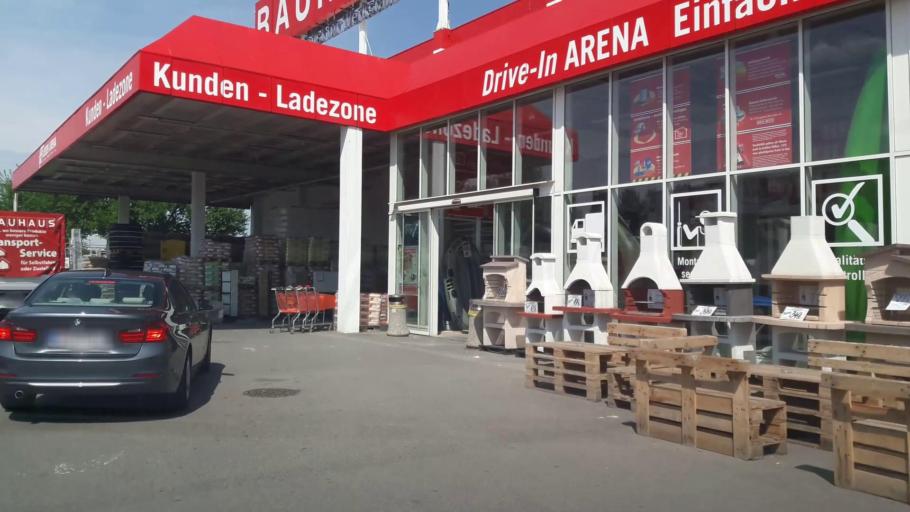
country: AT
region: Lower Austria
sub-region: Politischer Bezirk Modling
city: Vosendorf
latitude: 48.1495
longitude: 16.3607
